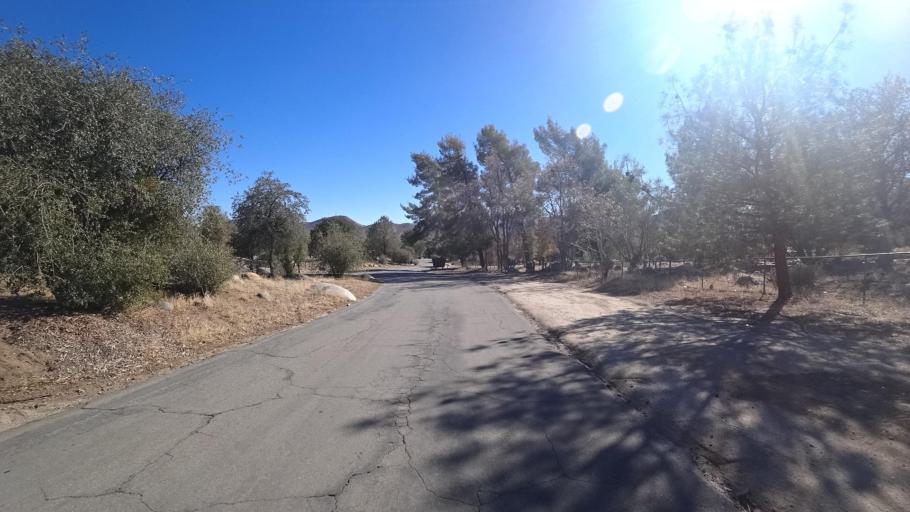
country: US
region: California
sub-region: Kern County
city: Wofford Heights
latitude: 35.7025
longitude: -118.4613
